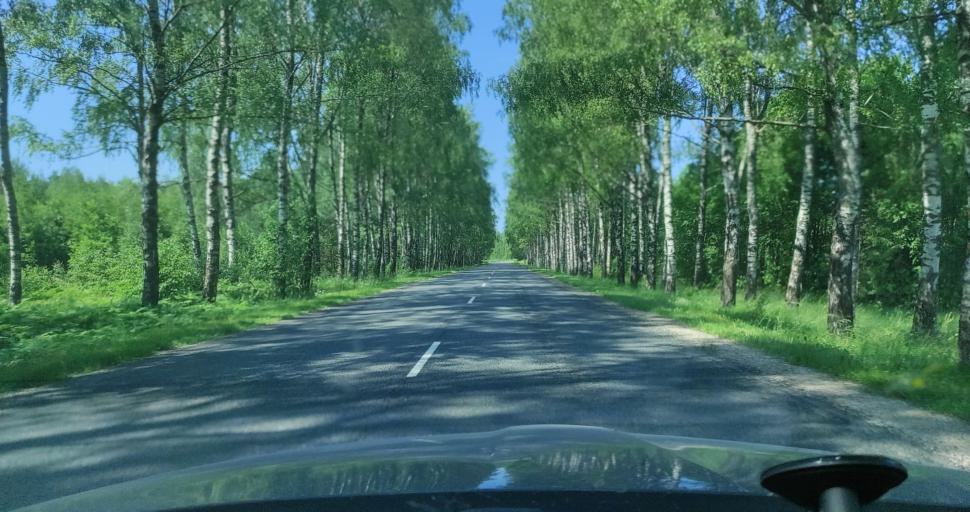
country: LV
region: Salacgrivas
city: Ainazi
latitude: 57.8595
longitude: 24.4989
